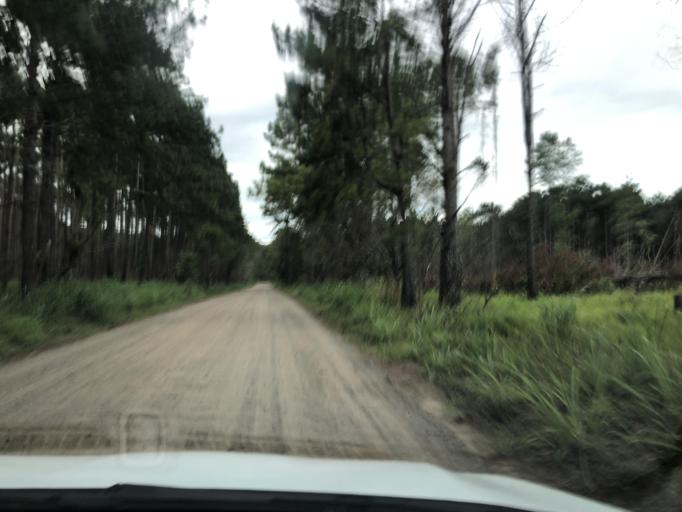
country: BR
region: Santa Catarina
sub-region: Florianopolis
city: Lagoa
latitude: -27.5492
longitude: -48.4410
